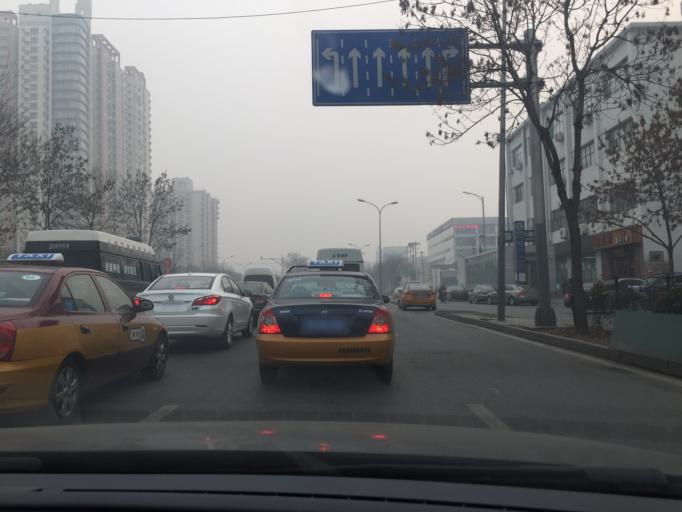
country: CN
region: Beijing
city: Qinghe
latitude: 40.0006
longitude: 116.3462
